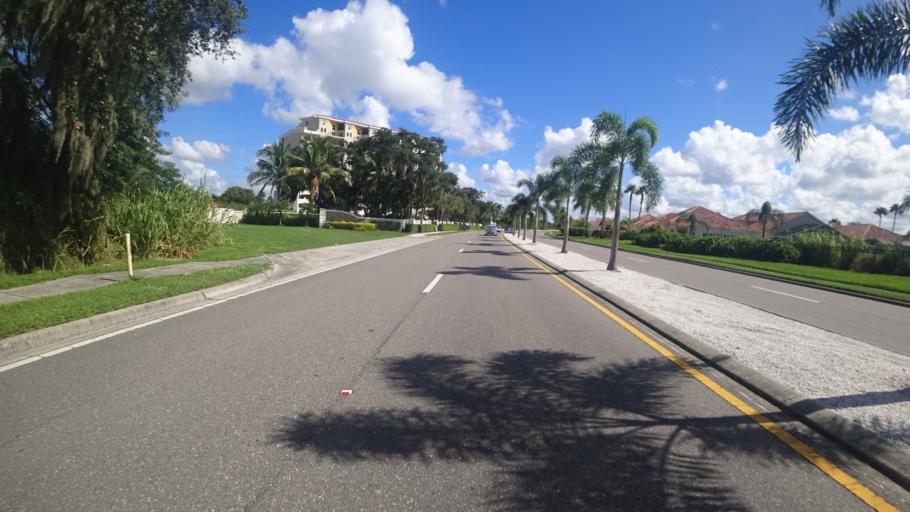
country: US
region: Florida
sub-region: Manatee County
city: Palmetto
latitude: 27.5162
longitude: -82.5583
